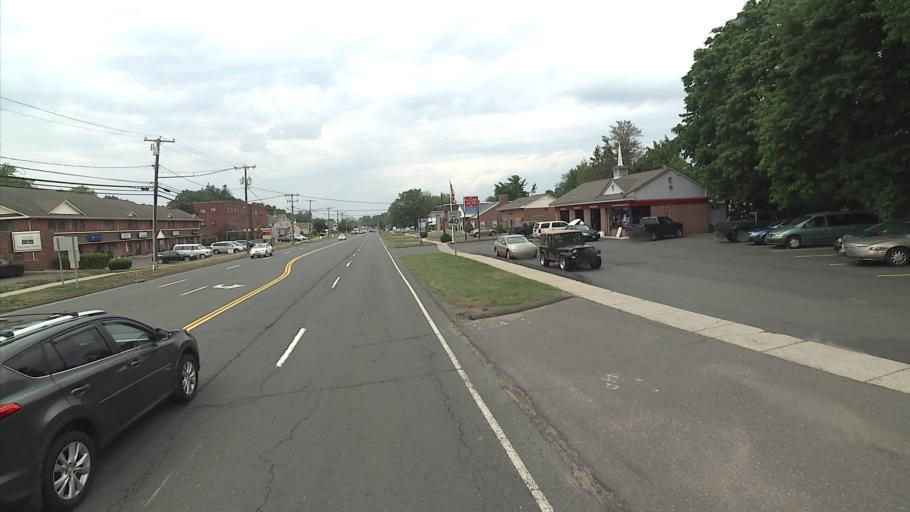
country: US
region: Connecticut
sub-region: Hartford County
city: Wethersfield
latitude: 41.6656
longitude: -72.6399
